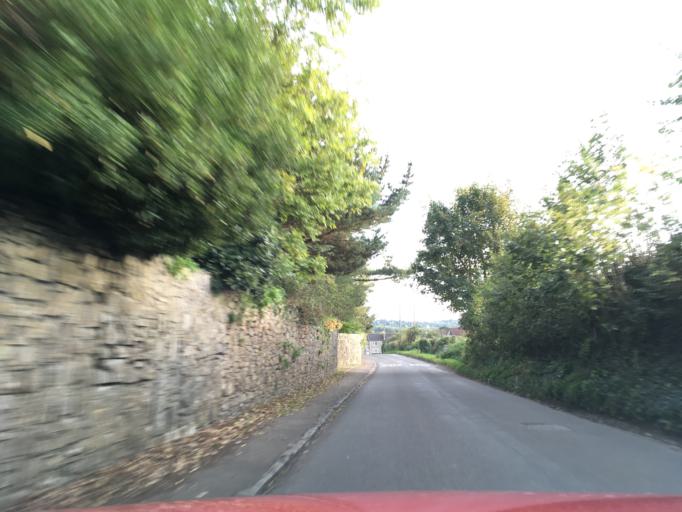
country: GB
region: England
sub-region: South Gloucestershire
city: Almondsbury
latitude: 51.5785
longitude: -2.5642
